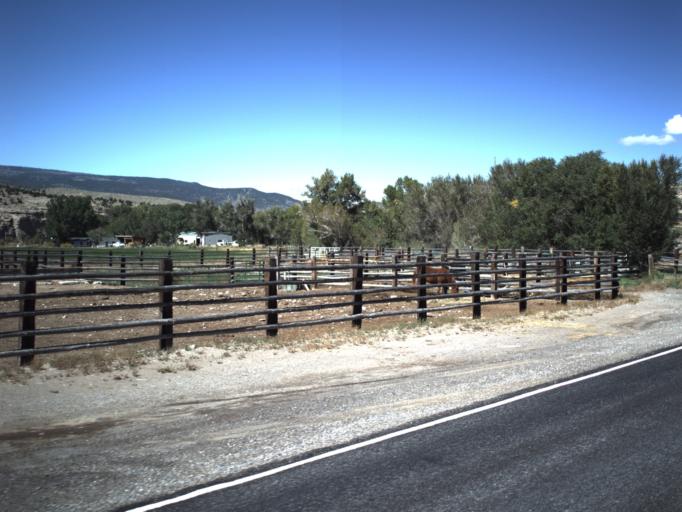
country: US
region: Utah
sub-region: Piute County
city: Junction
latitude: 38.0900
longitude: -111.9813
